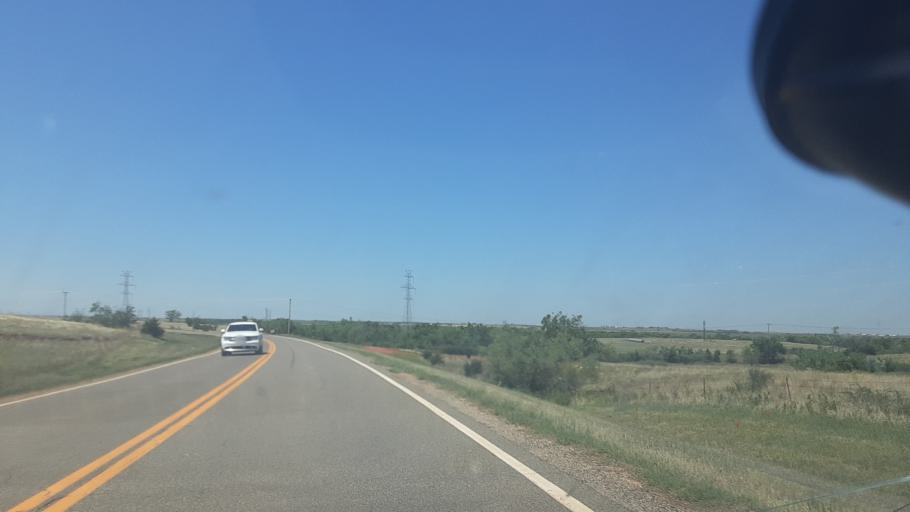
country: US
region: Oklahoma
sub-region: Noble County
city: Perry
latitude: 36.1157
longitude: -97.3689
